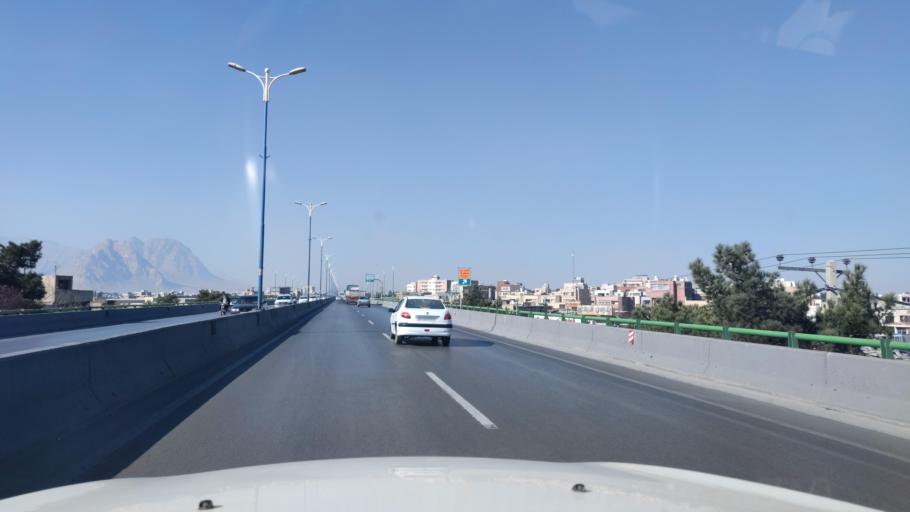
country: IR
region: Isfahan
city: Rehnan
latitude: 32.7061
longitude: 51.6096
